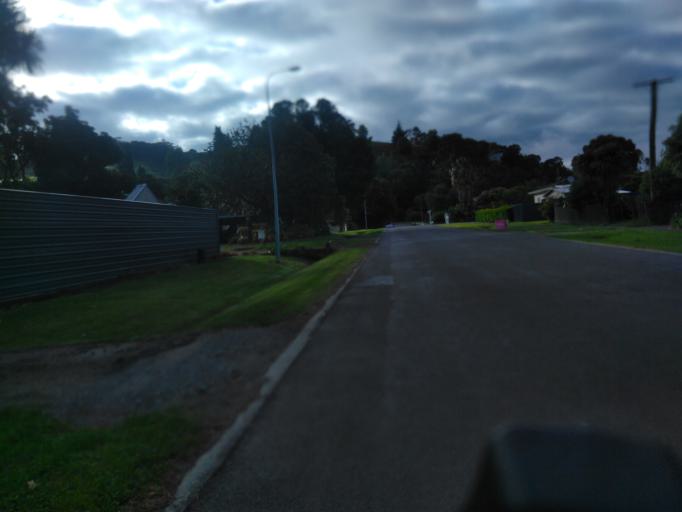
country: NZ
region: Gisborne
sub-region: Gisborne District
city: Gisborne
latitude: -38.6477
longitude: 178.0223
